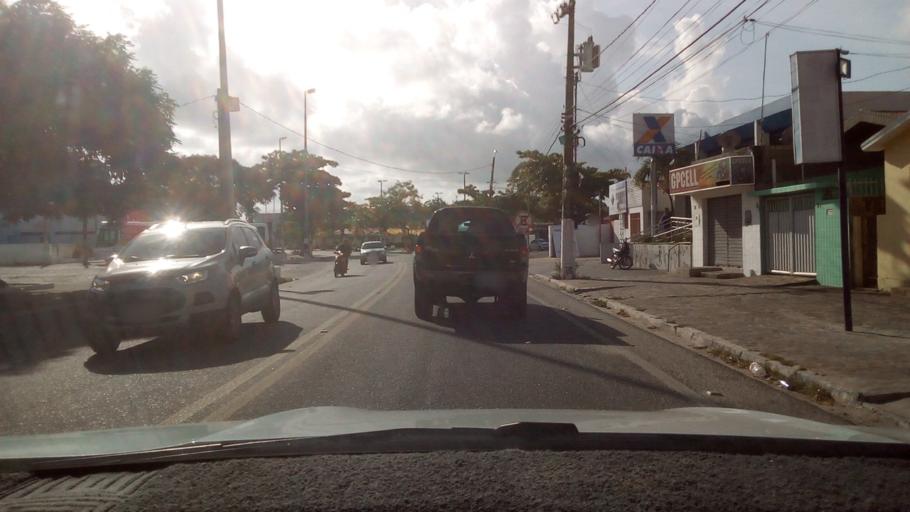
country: BR
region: Paraiba
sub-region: Cabedelo
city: Cabedelo
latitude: -6.9712
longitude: -34.8362
